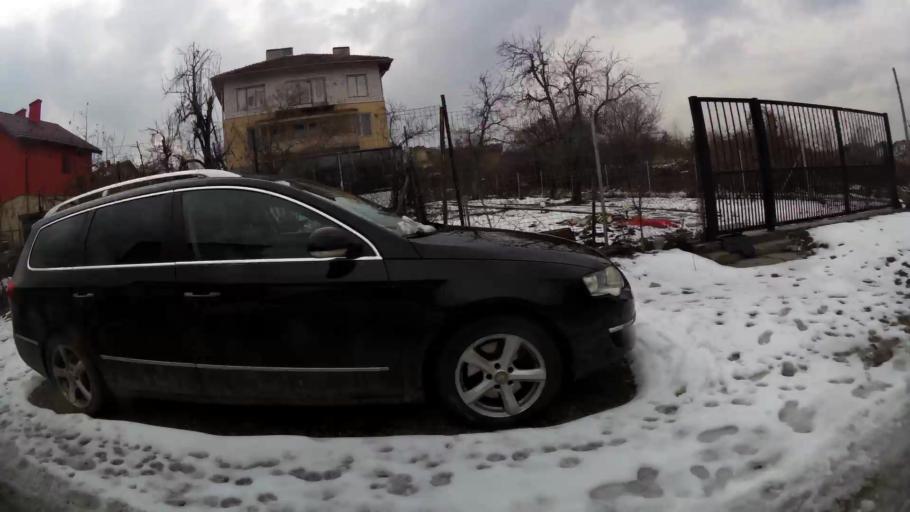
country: BG
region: Sofiya
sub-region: Obshtina Bozhurishte
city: Bozhurishte
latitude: 42.6802
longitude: 23.2383
